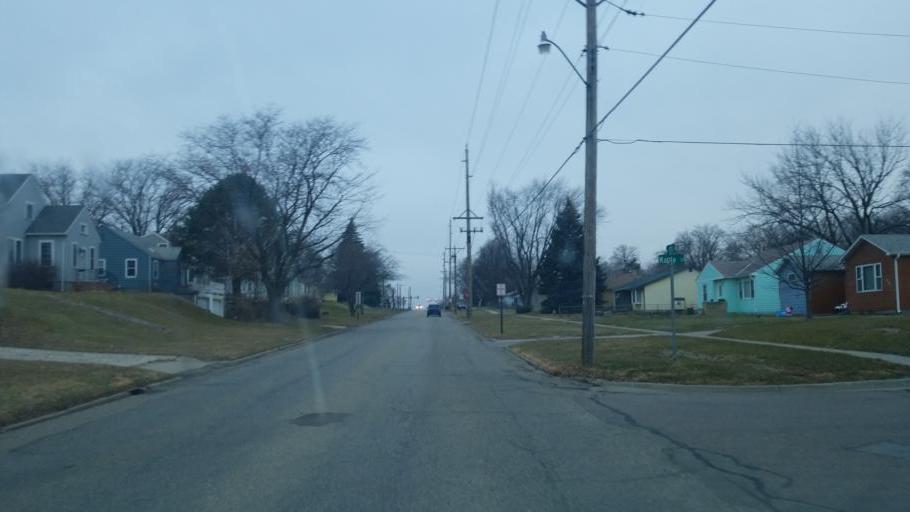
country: US
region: South Dakota
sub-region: Yankton County
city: Yankton
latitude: 42.8762
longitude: -97.4035
